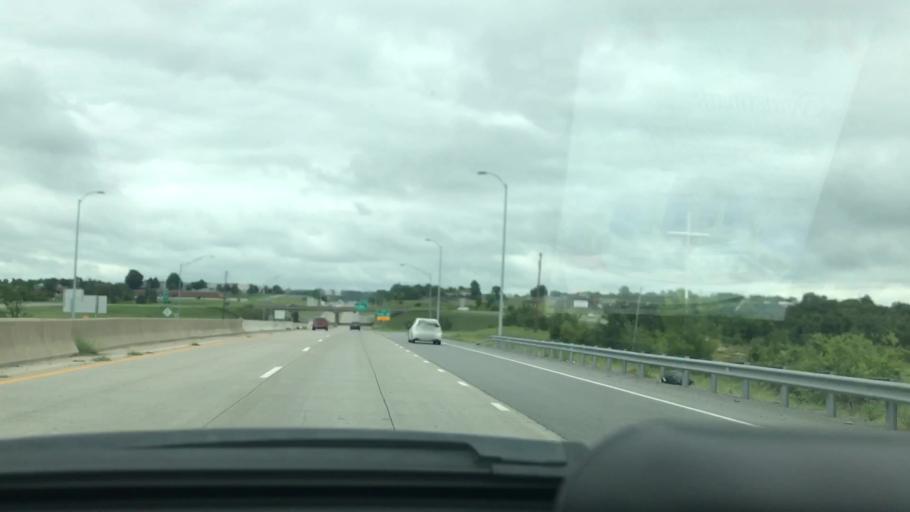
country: US
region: Oklahoma
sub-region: Pittsburg County
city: Krebs
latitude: 34.9246
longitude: -95.7421
